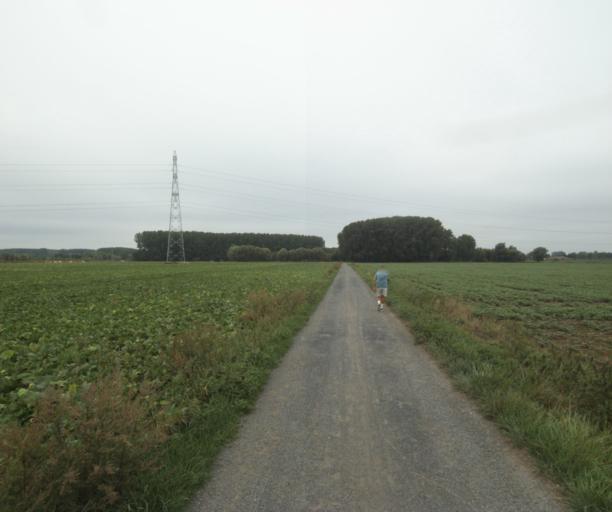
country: FR
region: Nord-Pas-de-Calais
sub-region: Departement du Nord
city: Willems
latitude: 50.6200
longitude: 3.2255
